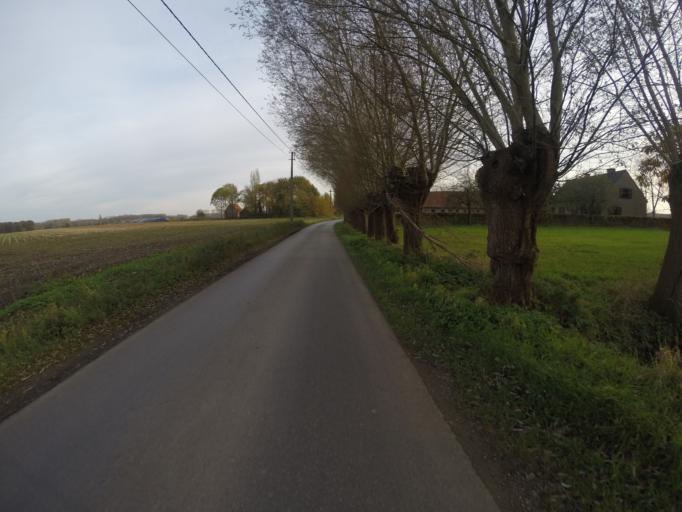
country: BE
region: Flanders
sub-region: Provincie Oost-Vlaanderen
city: Aalter
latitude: 51.0605
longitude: 3.4753
